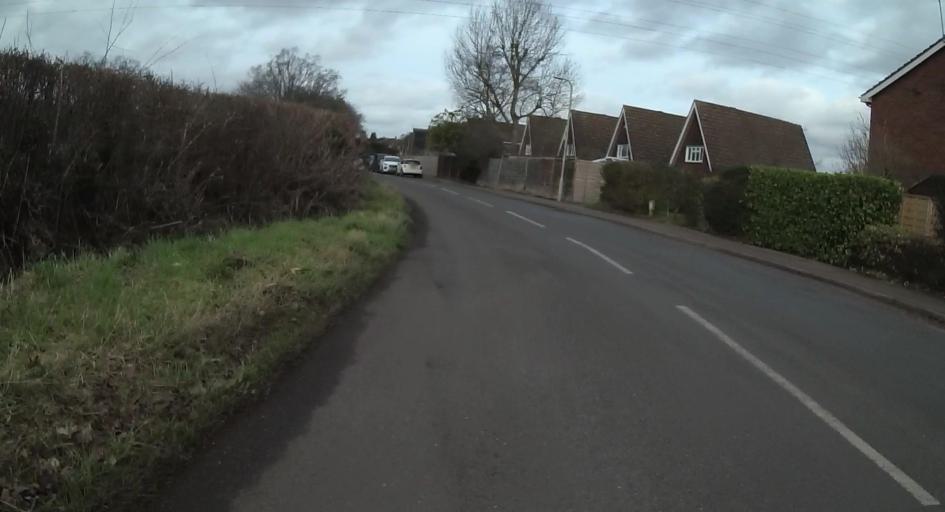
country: GB
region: England
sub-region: Wokingham
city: Wokingham
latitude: 51.4012
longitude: -0.8528
